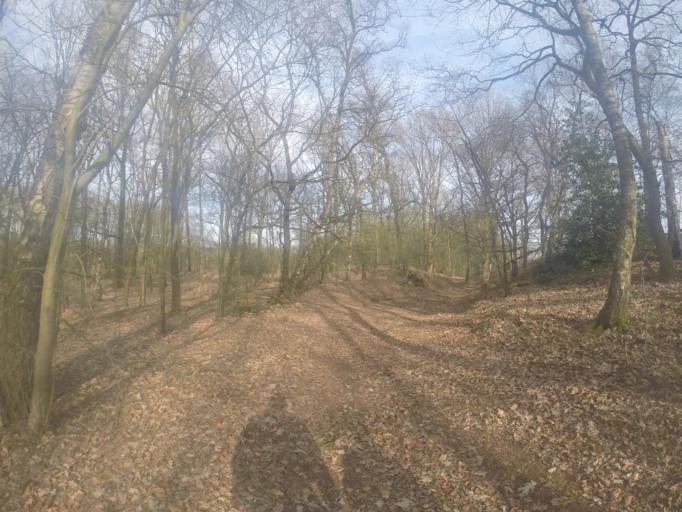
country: NL
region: Gelderland
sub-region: Gemeente Lochem
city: Lochem
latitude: 52.1262
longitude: 6.3701
